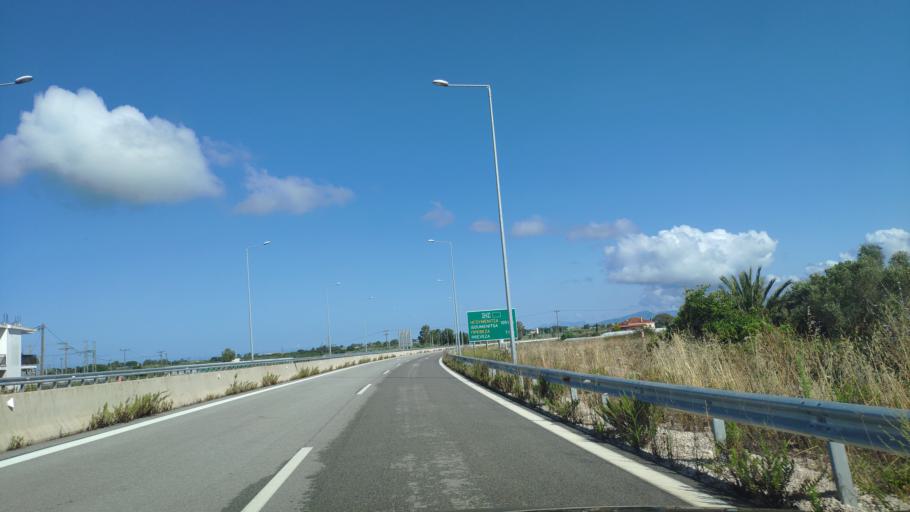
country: GR
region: Epirus
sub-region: Nomos Prevezis
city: Preveza
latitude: 38.9145
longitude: 20.7945
